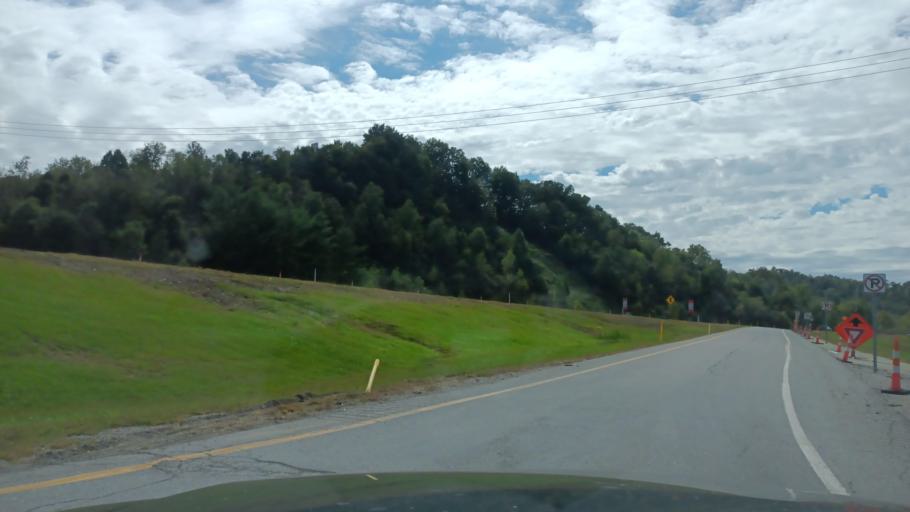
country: US
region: West Virginia
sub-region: Ritchie County
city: Harrisville
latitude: 39.2641
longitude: -81.0560
